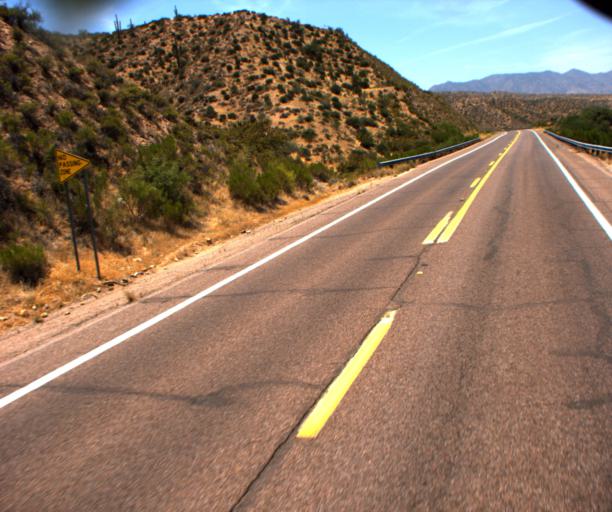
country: US
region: Arizona
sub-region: Gila County
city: Tonto Basin
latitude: 33.7541
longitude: -111.2439
